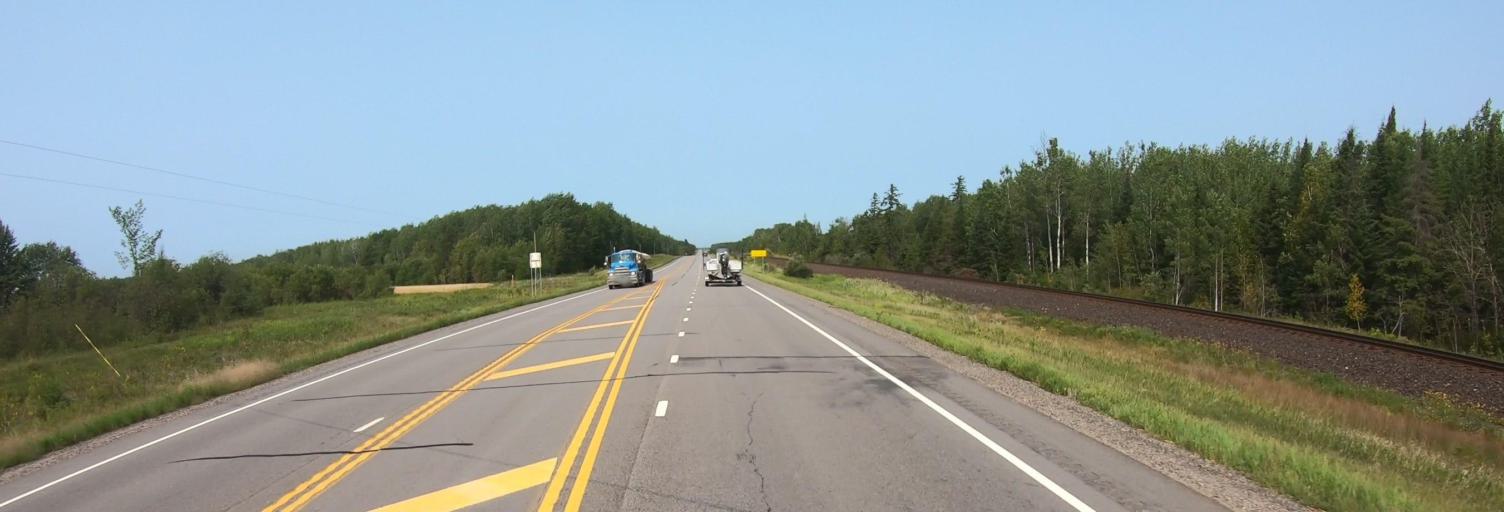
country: CA
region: Ontario
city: Fort Frances
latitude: 48.4480
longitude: -93.2667
